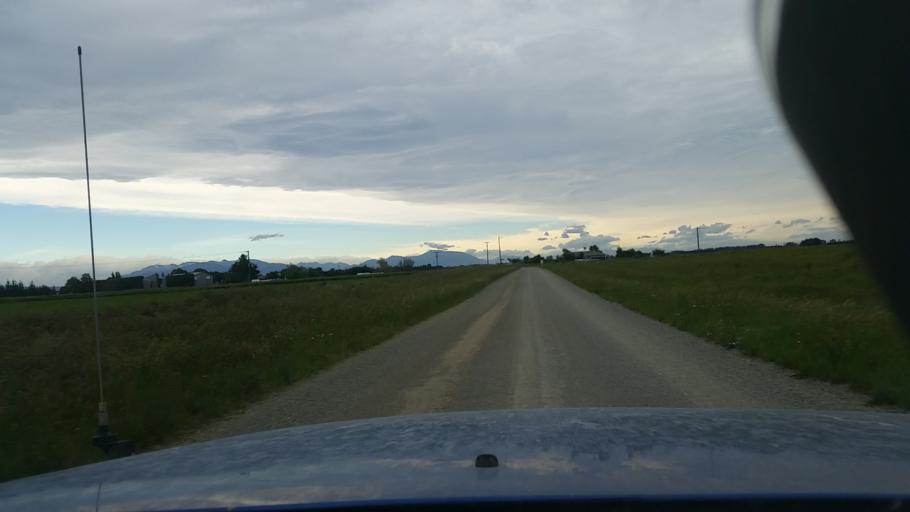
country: NZ
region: Canterbury
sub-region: Ashburton District
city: Tinwald
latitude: -43.9778
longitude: 171.5081
